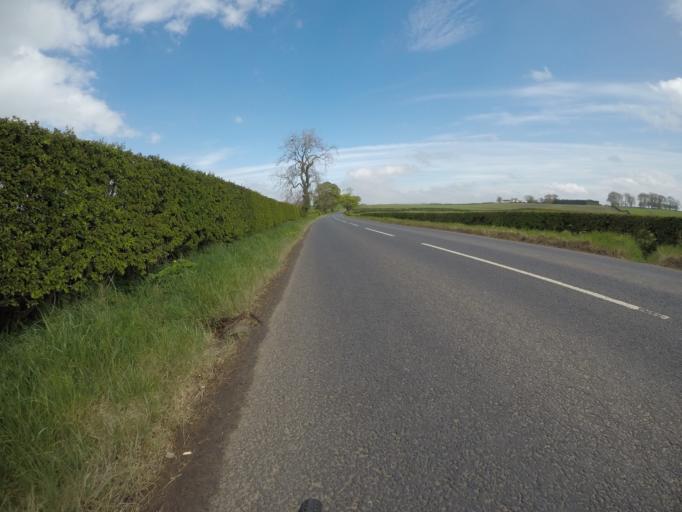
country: GB
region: Scotland
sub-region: East Ayrshire
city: Crosshouse
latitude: 55.6505
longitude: -4.5688
